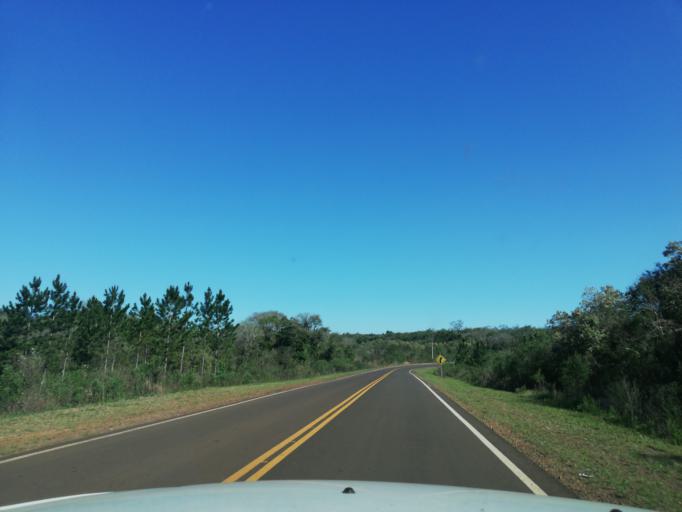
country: AR
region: Misiones
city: Arroyo del Medio
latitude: -27.6851
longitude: -55.3971
